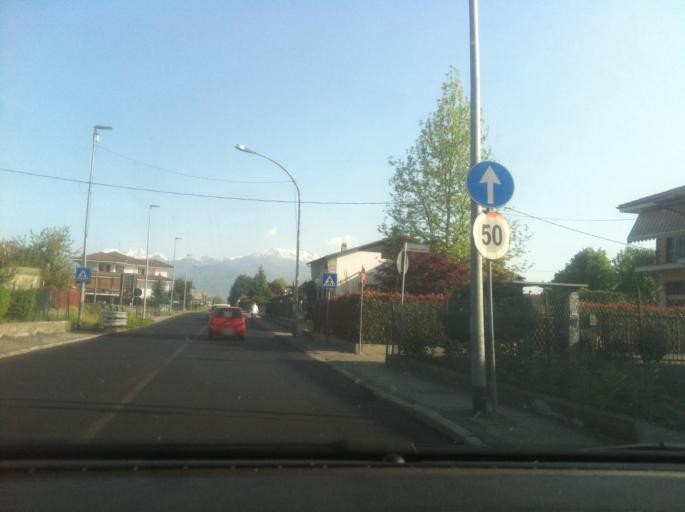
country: IT
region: Piedmont
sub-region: Provincia di Torino
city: Strambino
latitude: 45.3852
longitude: 7.8854
